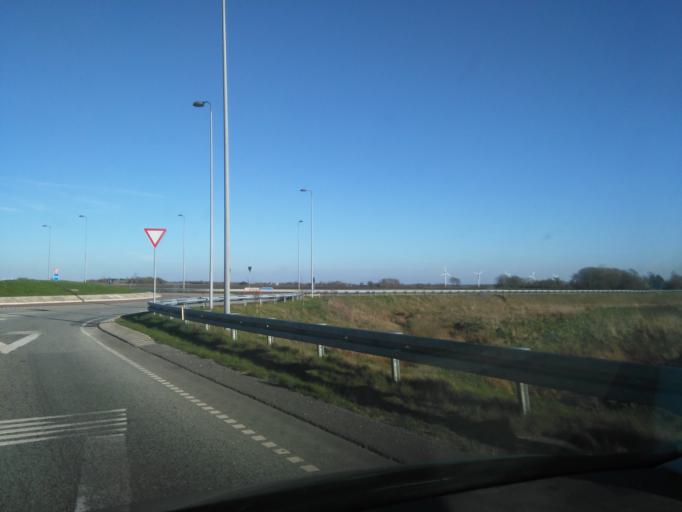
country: DK
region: Central Jutland
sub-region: Herning Kommune
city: Snejbjerg
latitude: 56.1278
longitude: 8.8728
